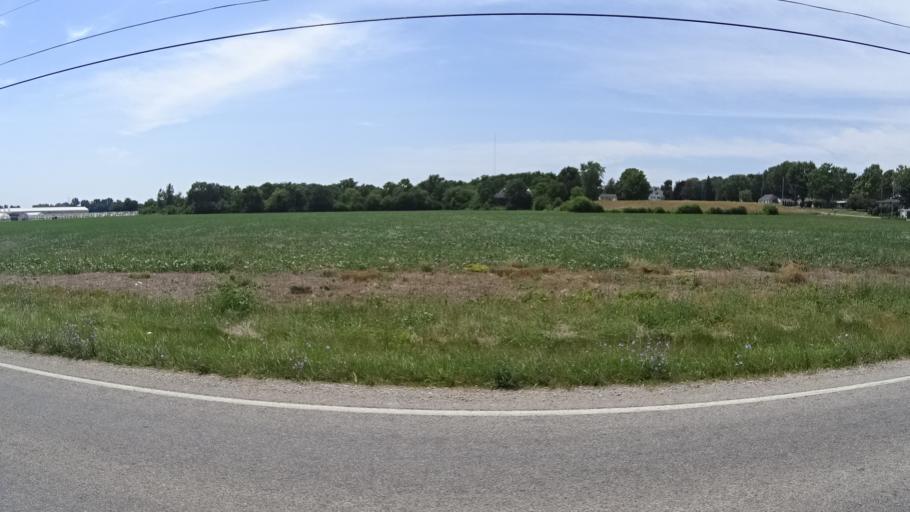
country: US
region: Ohio
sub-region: Erie County
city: Sandusky
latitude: 41.3970
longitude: -82.7710
